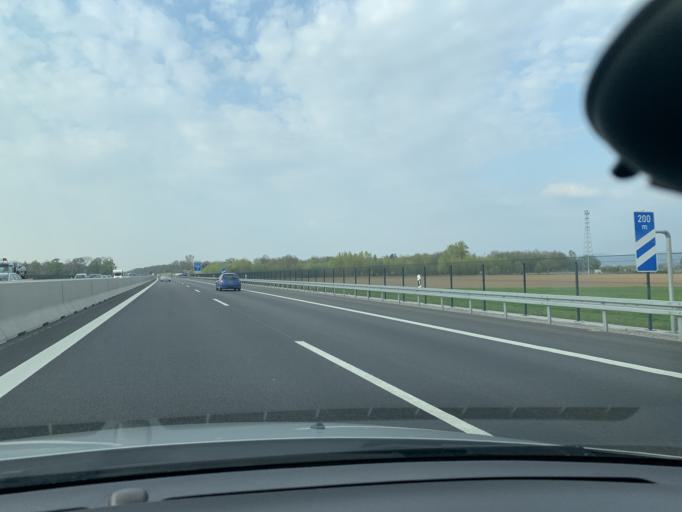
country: DE
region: Baden-Wuerttemberg
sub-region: Freiburg Region
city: Mahlberg
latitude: 48.3022
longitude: 7.7899
